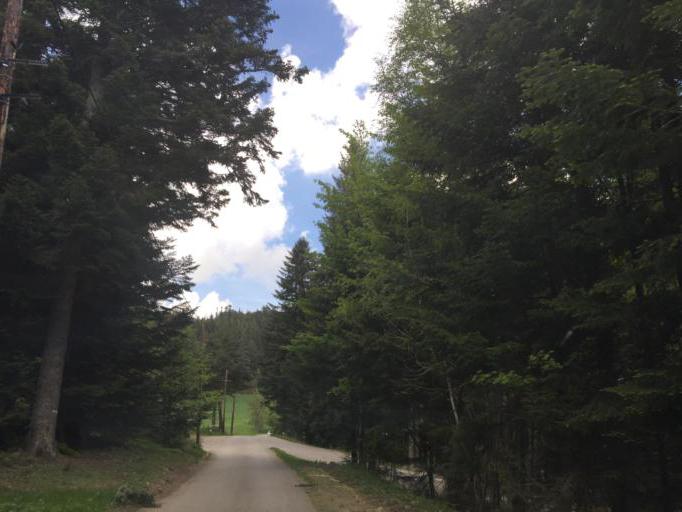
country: FR
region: Rhone-Alpes
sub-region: Departement de la Loire
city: Saint-Sauveur-en-Rue
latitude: 45.2743
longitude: 4.4731
